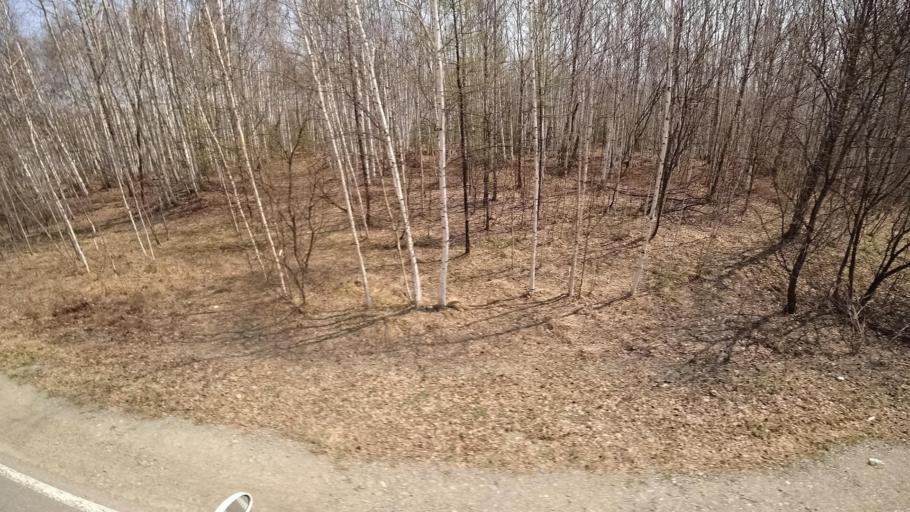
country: RU
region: Khabarovsk Krai
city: Selikhino
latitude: 50.3951
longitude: 137.3737
